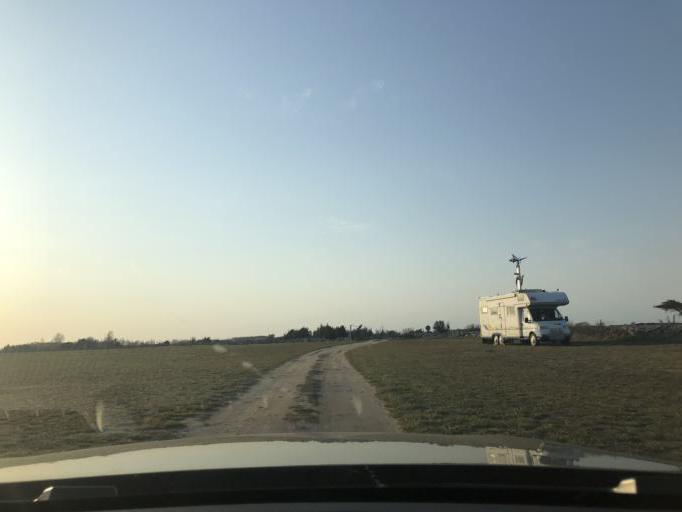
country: SE
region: Kalmar
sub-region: Morbylanga Kommun
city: Sodra Sandby
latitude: 56.5539
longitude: 16.6412
